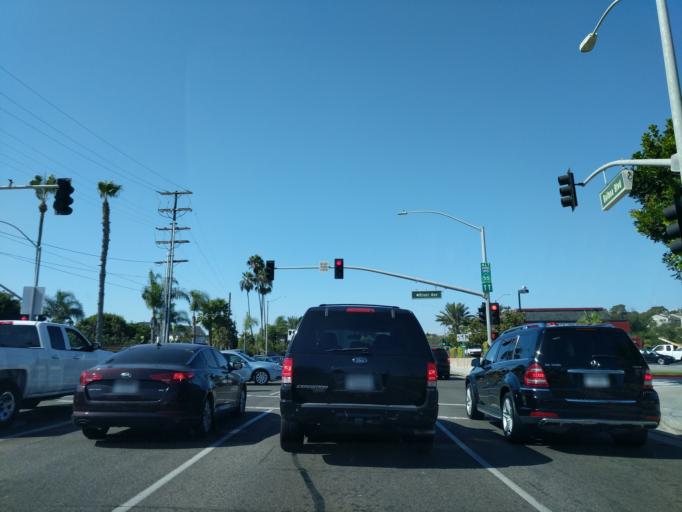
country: US
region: California
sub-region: Orange County
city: Newport Beach
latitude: 33.6218
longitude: -117.9388
